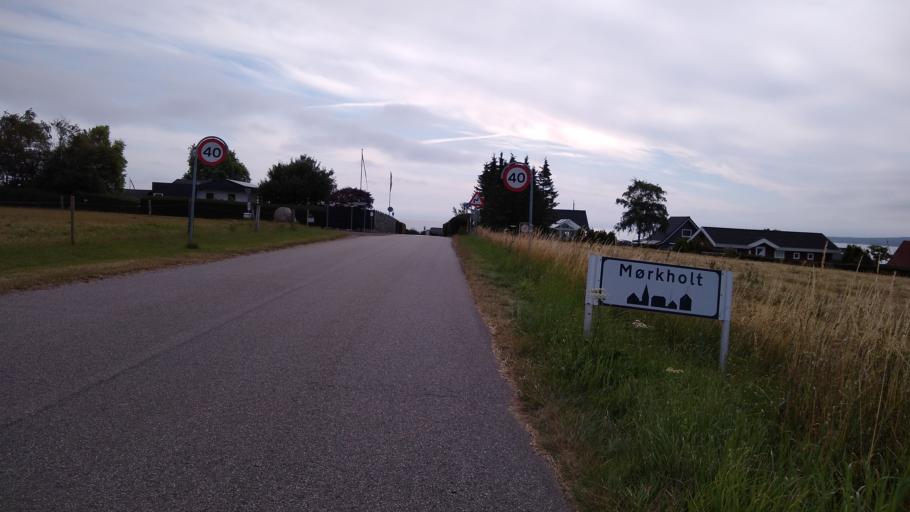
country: DK
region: South Denmark
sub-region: Vejle Kommune
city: Brejning
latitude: 55.6496
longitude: 9.7380
